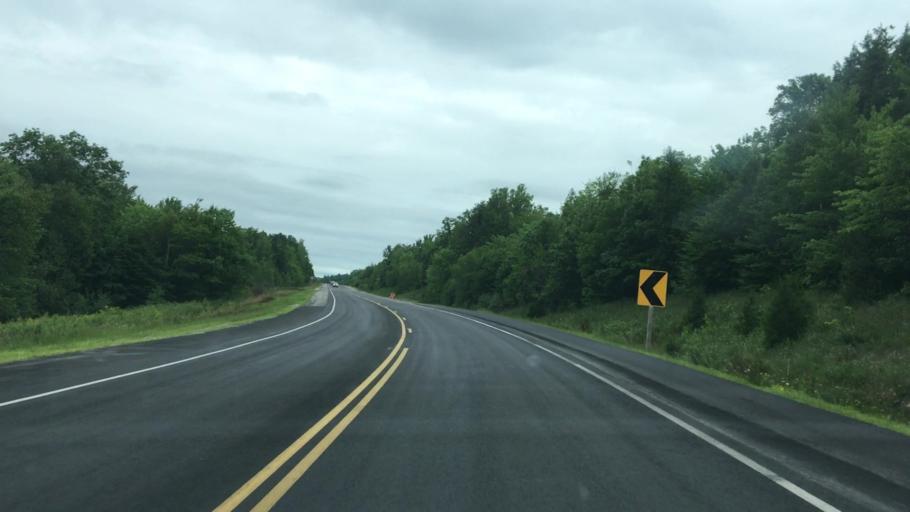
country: US
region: Maine
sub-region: Washington County
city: Cherryfield
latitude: 44.8840
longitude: -67.8572
